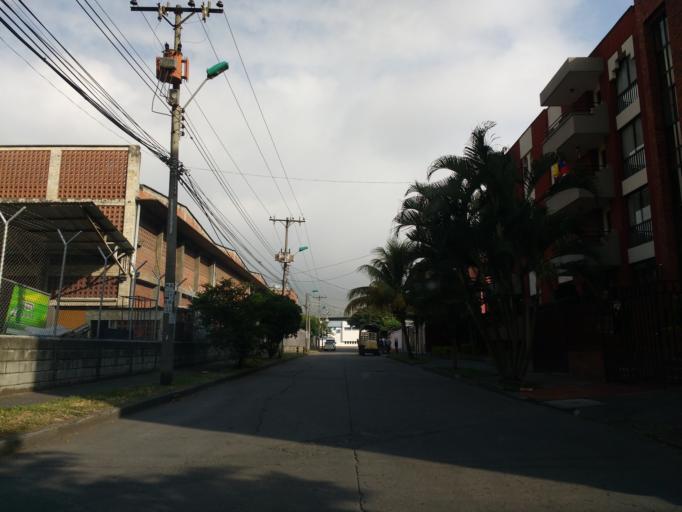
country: CO
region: Valle del Cauca
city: Cali
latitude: 3.4704
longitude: -76.5191
